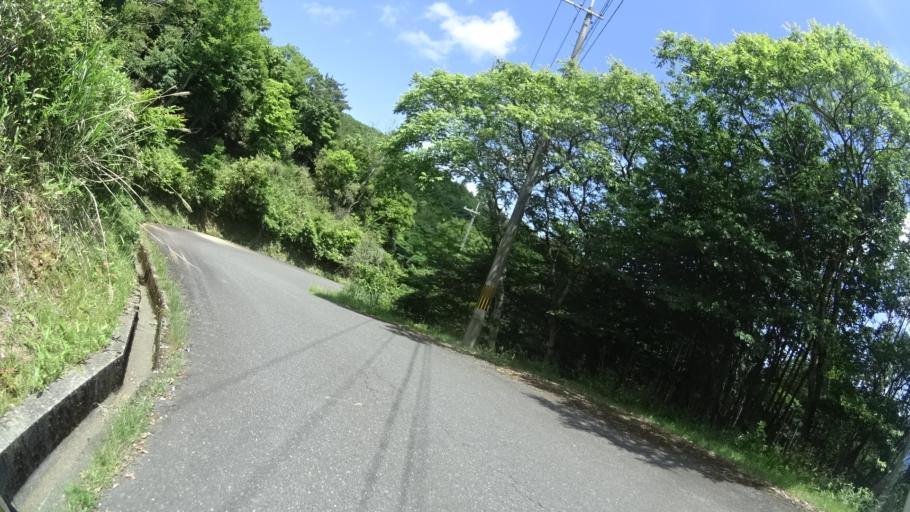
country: JP
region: Kyoto
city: Miyazu
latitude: 35.4725
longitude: 135.1641
